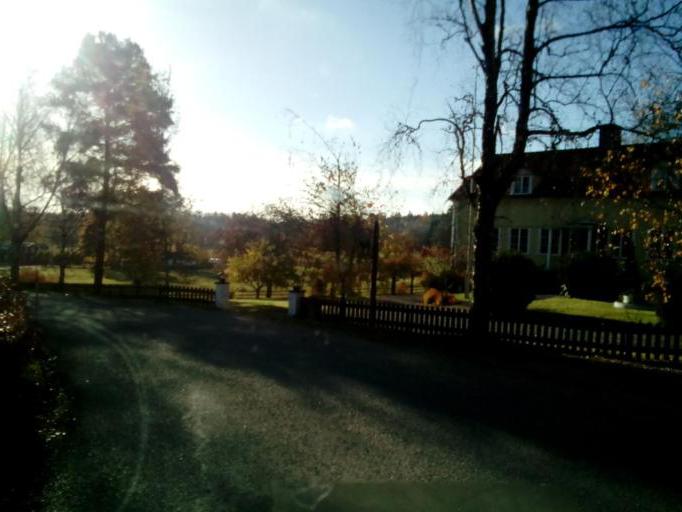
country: SE
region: Kalmar
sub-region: Vasterviks Kommun
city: Ankarsrum
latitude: 57.8228
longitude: 16.1462
